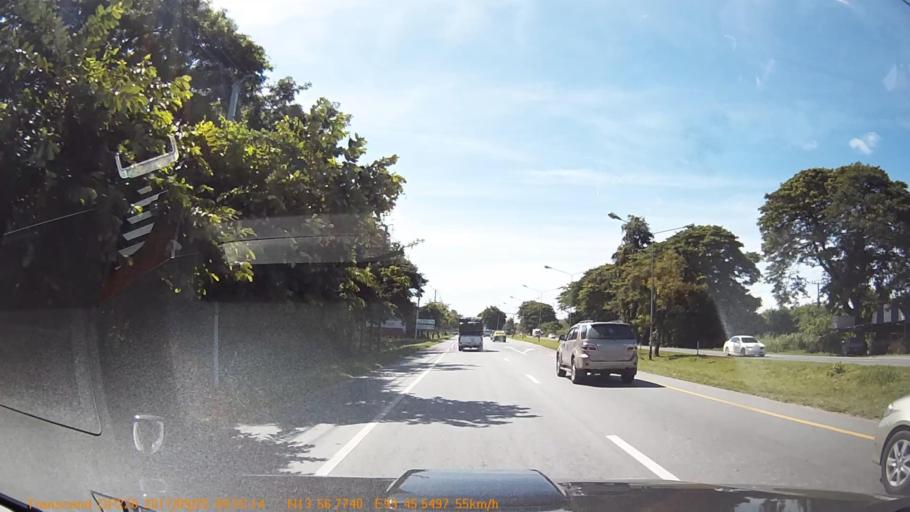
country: TH
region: Kanchanaburi
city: Tha Maka
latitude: 13.9460
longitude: 99.7592
